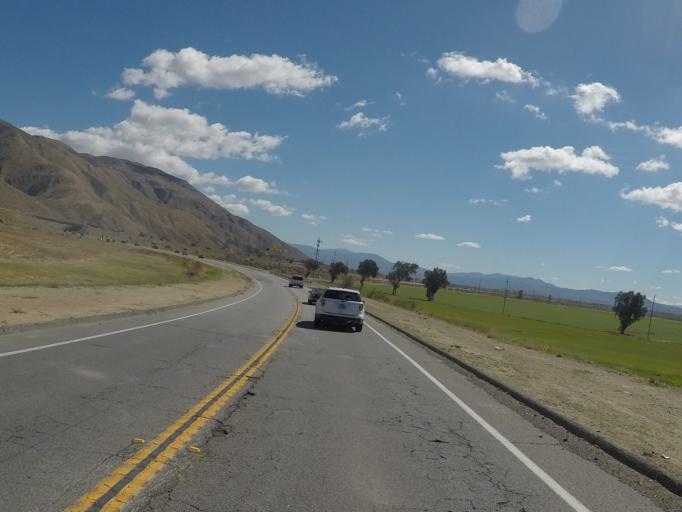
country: US
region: California
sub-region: Riverside County
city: San Jacinto
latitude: 33.8467
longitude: -117.0097
